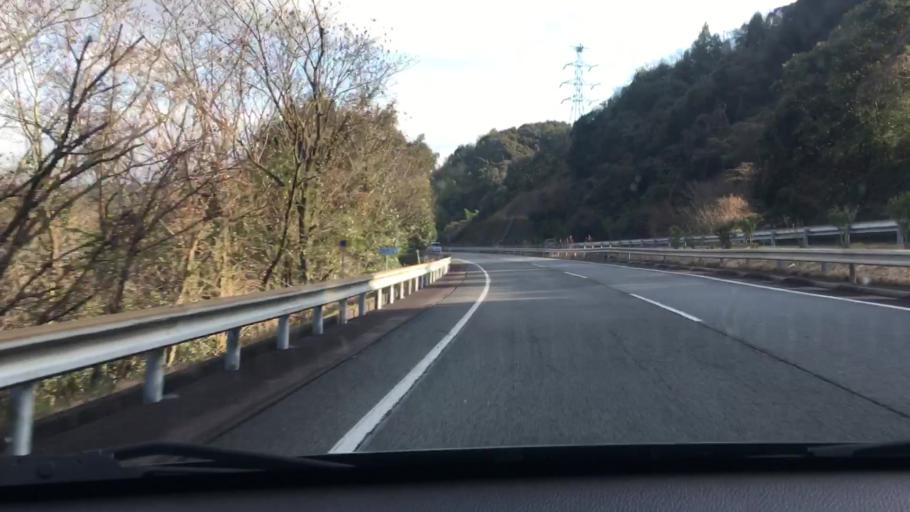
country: JP
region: Kumamoto
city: Hitoyoshi
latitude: 32.2682
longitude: 130.7617
